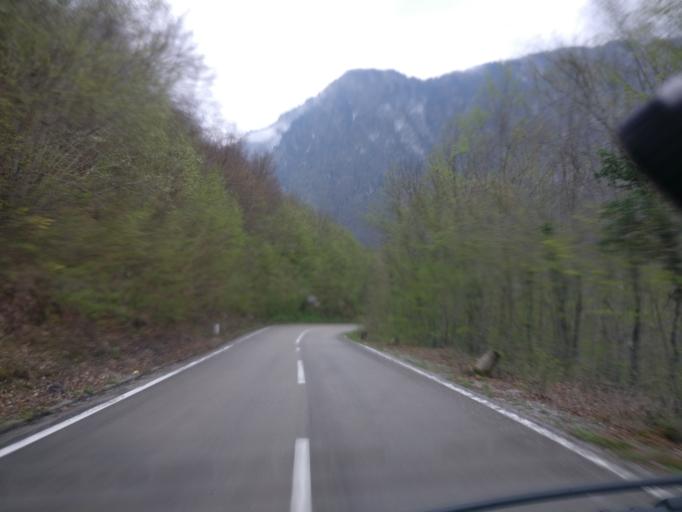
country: ME
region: Opstina Pluzine
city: Pluzine
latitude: 43.3119
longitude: 18.8550
